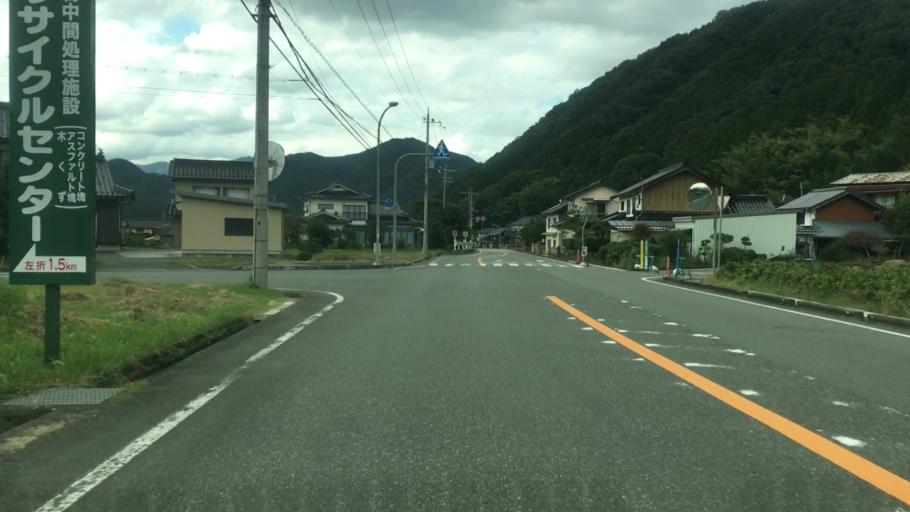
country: JP
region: Kyoto
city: Fukuchiyama
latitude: 35.3100
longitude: 134.8965
